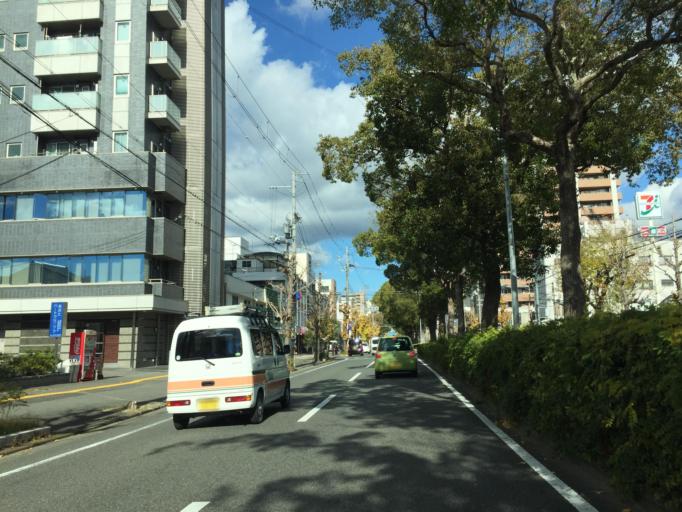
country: JP
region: Wakayama
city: Wakayama-shi
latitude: 34.2268
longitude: 135.1782
